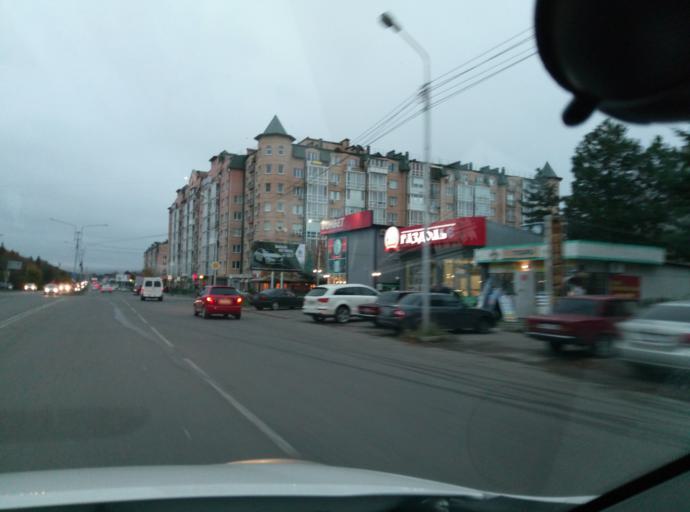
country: RU
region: Stavropol'skiy
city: Yessentukskaya
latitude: 44.0495
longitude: 42.8942
